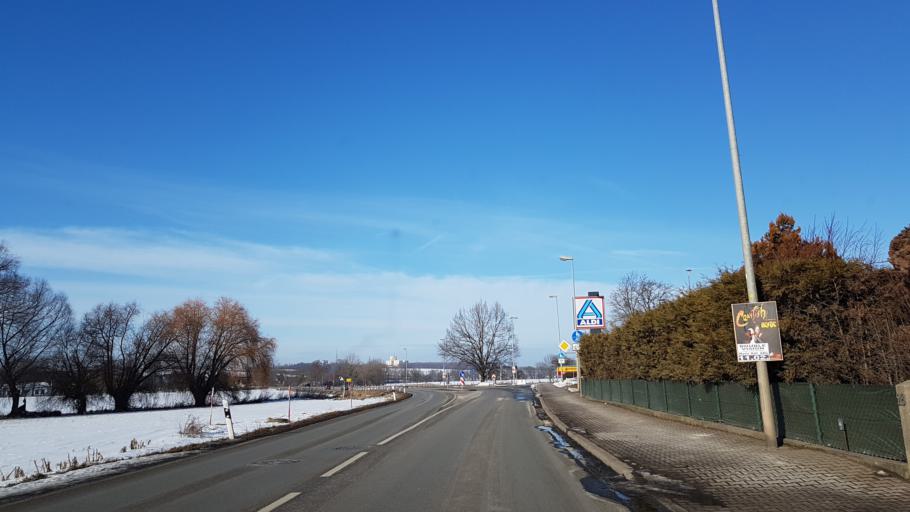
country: DE
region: Thuringia
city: Nobitz
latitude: 50.9795
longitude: 12.4836
